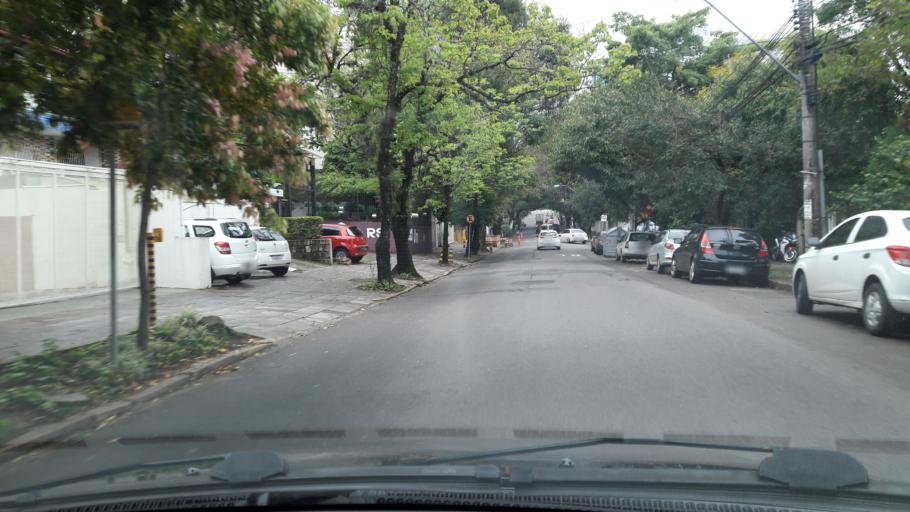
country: BR
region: Rio Grande do Sul
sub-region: Porto Alegre
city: Porto Alegre
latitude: -30.0281
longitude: -51.1842
